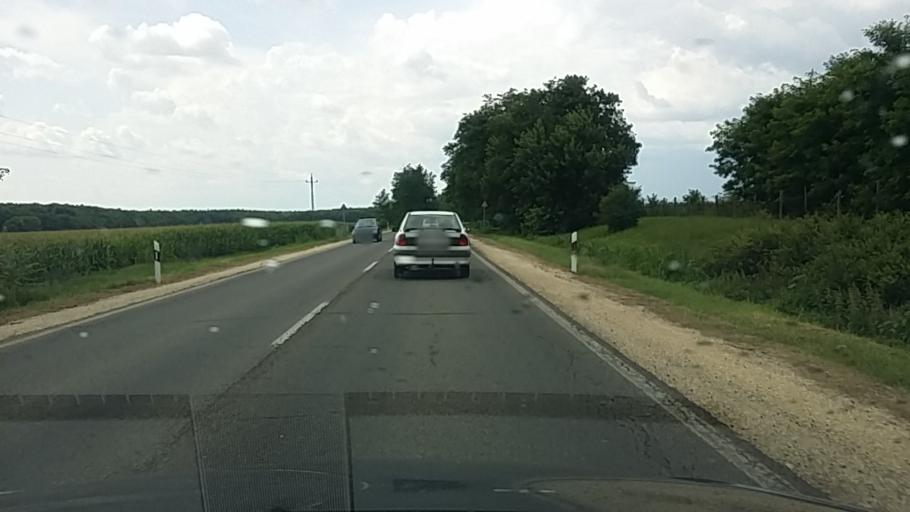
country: HU
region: Pest
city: Orkeny
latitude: 47.1404
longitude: 19.4035
